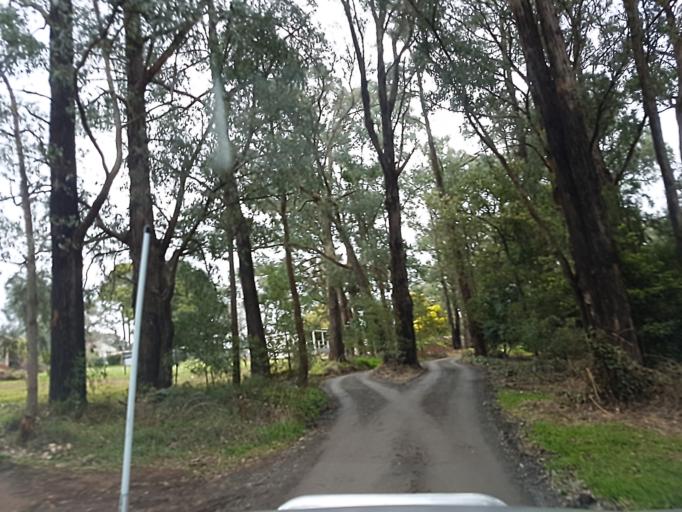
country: AU
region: Victoria
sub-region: Yarra Ranges
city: Monbulk
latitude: -37.8824
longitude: 145.4233
